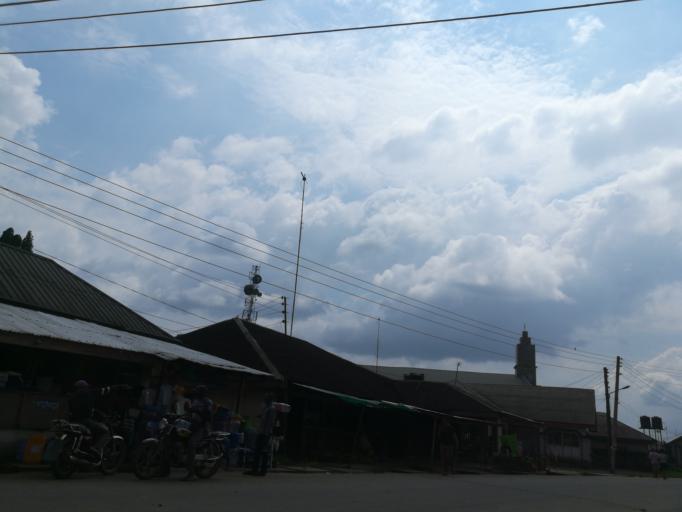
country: NG
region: Rivers
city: Okrika
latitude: 4.7270
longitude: 7.1522
